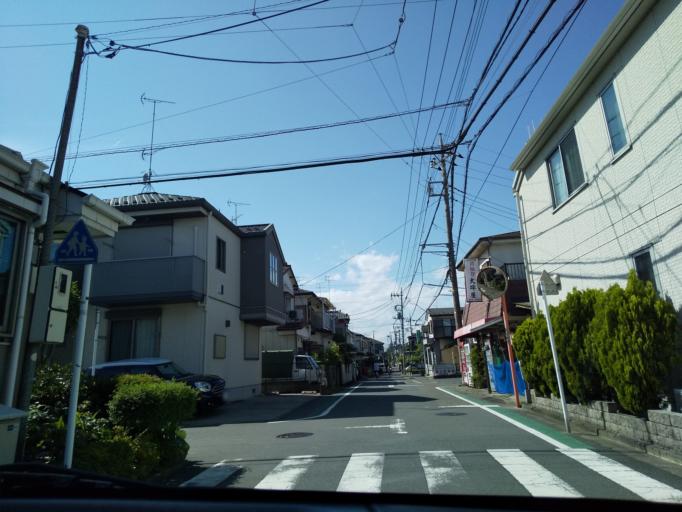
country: JP
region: Kanagawa
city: Zama
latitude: 35.5492
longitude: 139.3833
